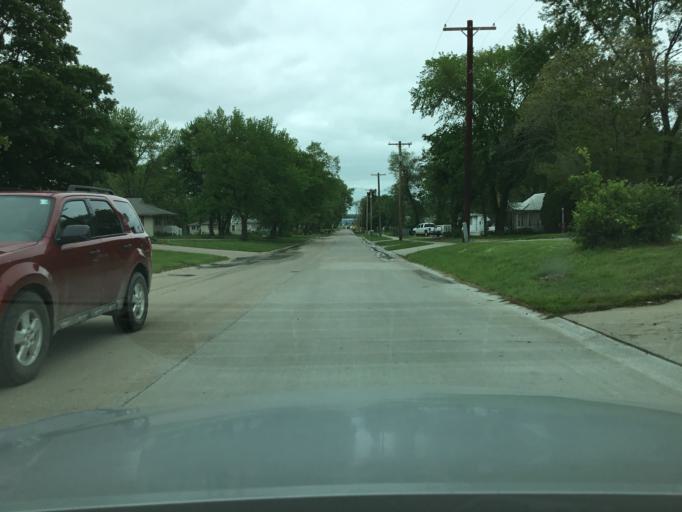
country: US
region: Kansas
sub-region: Franklin County
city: Ottawa
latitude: 38.6310
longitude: -95.2586
